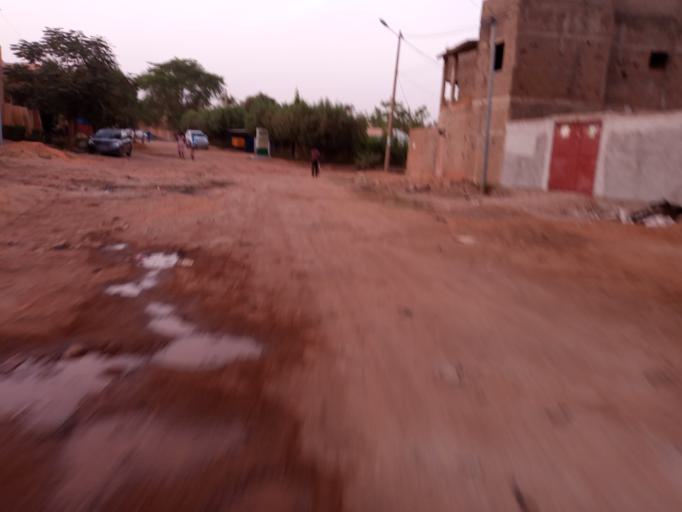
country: ML
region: Bamako
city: Bamako
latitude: 12.5831
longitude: -7.9496
